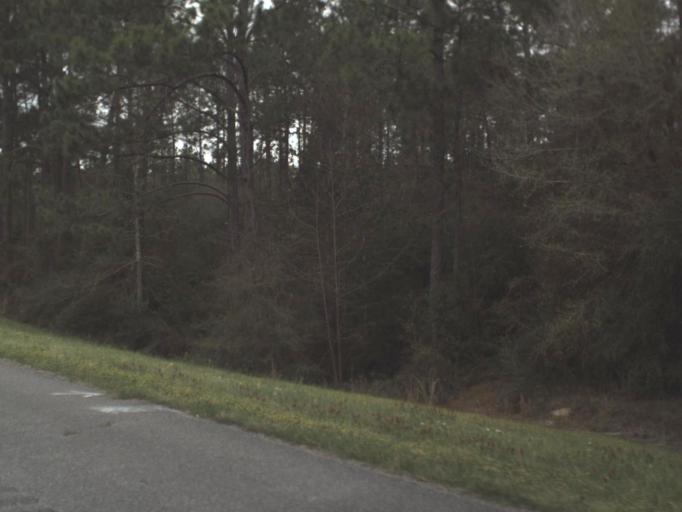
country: US
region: Florida
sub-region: Okaloosa County
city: Crestview
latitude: 30.7272
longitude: -86.5415
